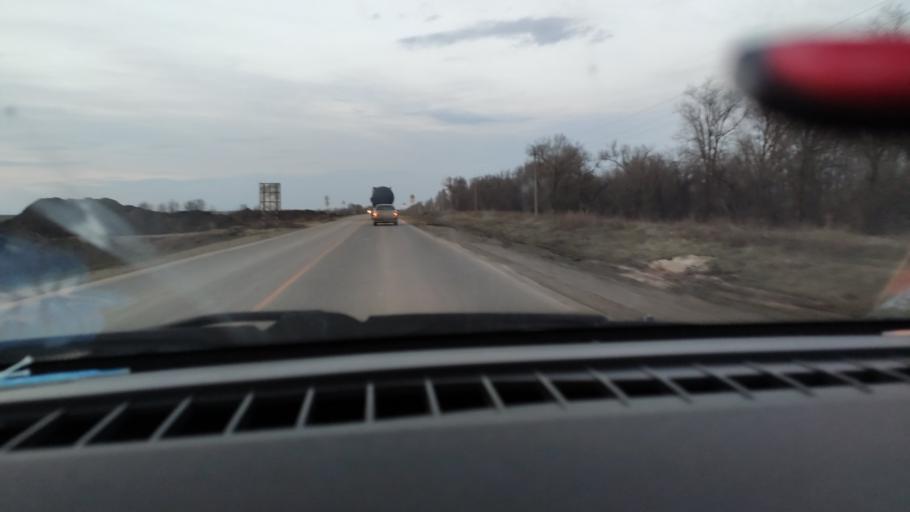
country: RU
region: Saratov
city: Sinodskoye
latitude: 52.0171
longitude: 46.7000
